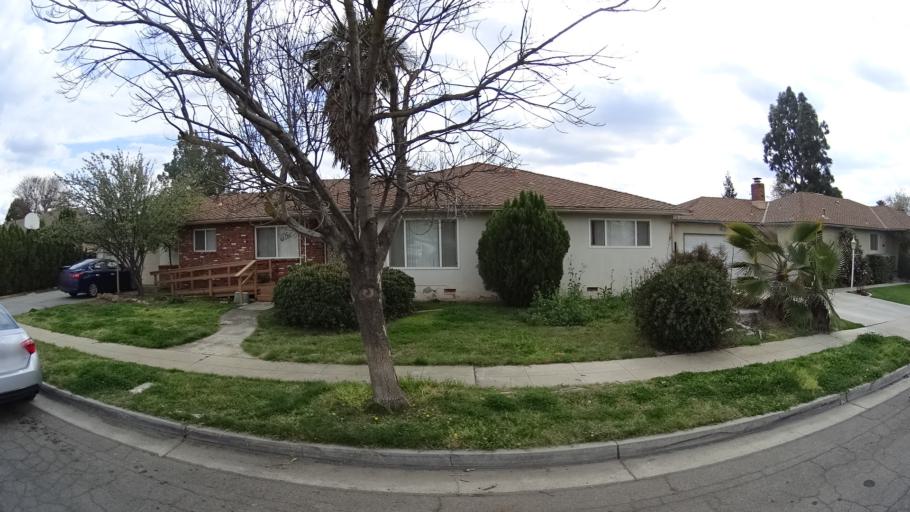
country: US
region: California
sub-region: Fresno County
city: Clovis
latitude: 36.8310
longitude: -119.7703
